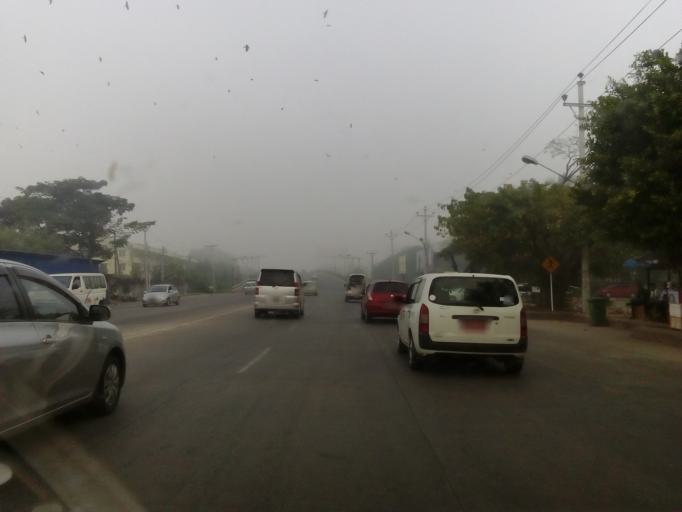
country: MM
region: Yangon
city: Yangon
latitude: 16.8154
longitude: 96.1902
